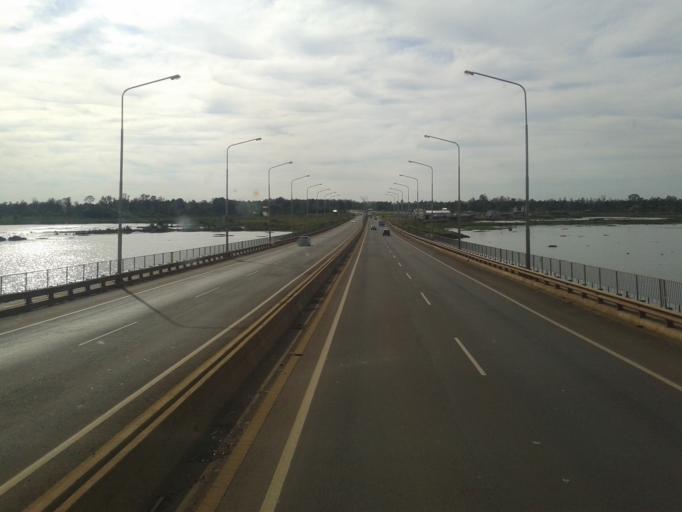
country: AR
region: Misiones
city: Garupa
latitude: -27.4632
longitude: -55.8124
